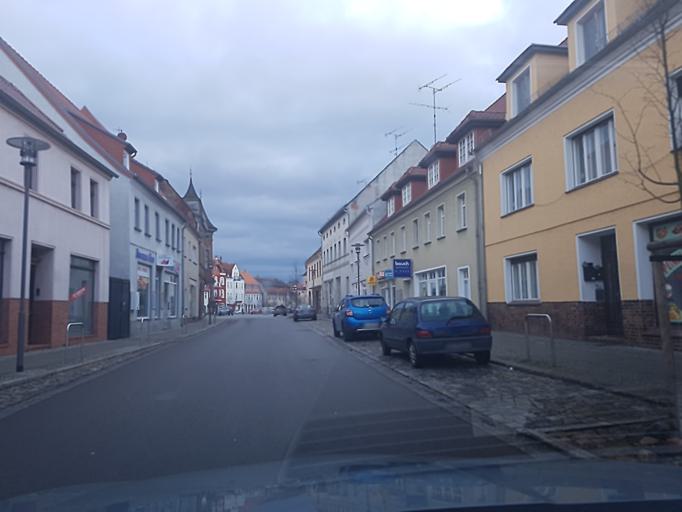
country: DE
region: Brandenburg
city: Doberlug-Kirchhain
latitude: 51.6384
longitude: 13.5624
